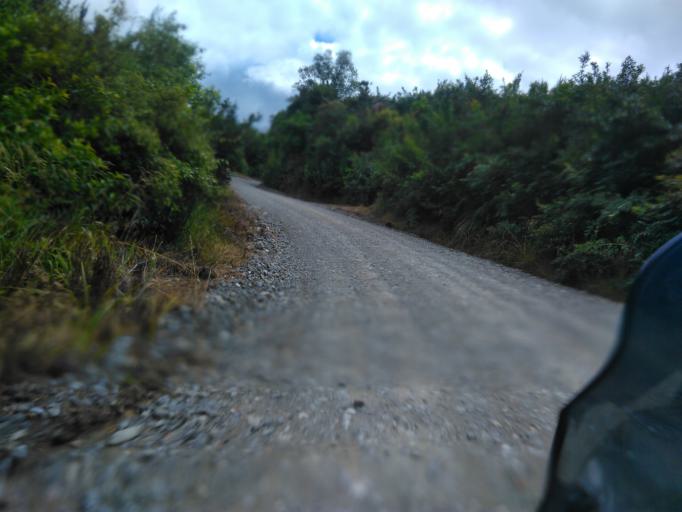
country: NZ
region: Gisborne
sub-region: Gisborne District
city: Gisborne
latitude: -38.1804
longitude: 178.1253
